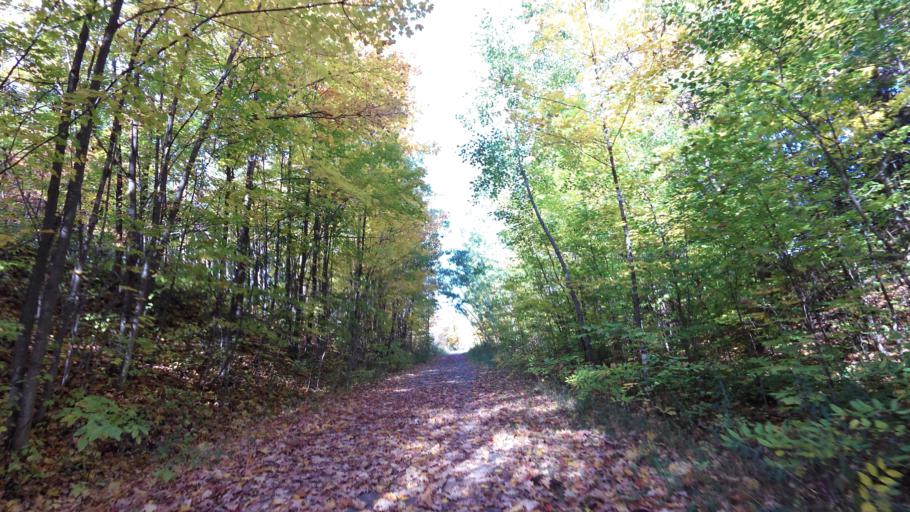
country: CA
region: Ontario
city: Orangeville
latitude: 43.8073
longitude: -80.0323
